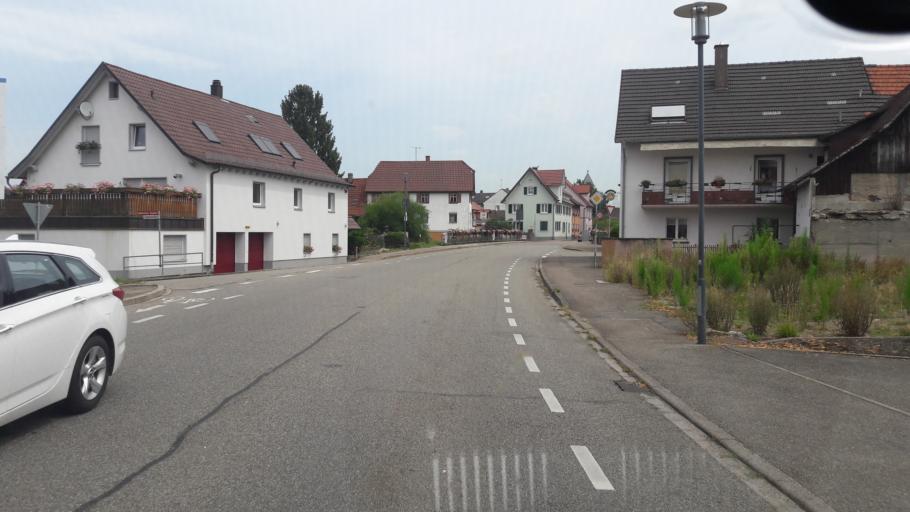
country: DE
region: Baden-Wuerttemberg
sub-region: Freiburg Region
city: Renchen
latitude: 48.5847
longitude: 8.0076
